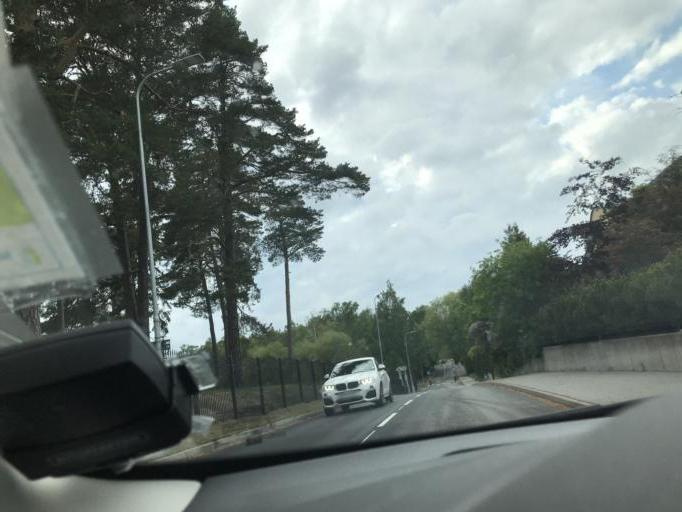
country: SE
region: Stockholm
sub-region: Botkyrka Kommun
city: Tumba
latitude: 59.1950
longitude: 17.8036
